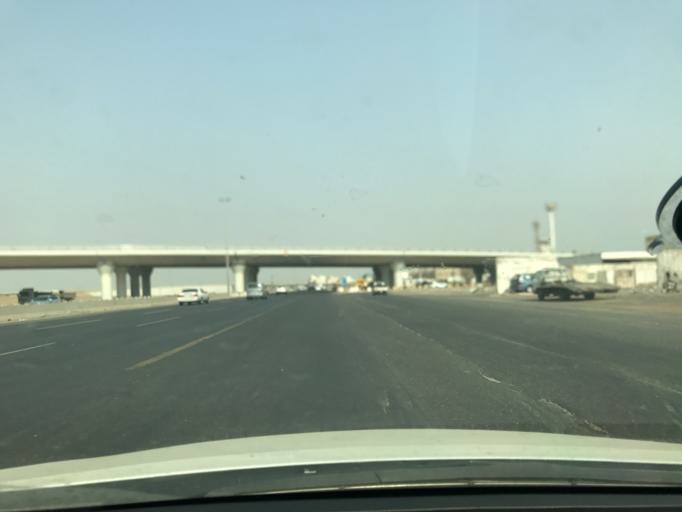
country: SA
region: Makkah
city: Jeddah
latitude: 21.6321
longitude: 39.1721
